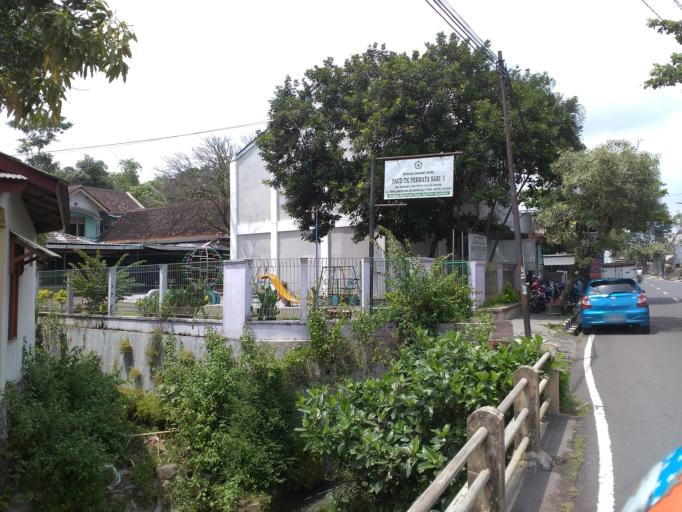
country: ID
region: Central Java
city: Boyolali
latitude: -7.5388
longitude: 110.6036
